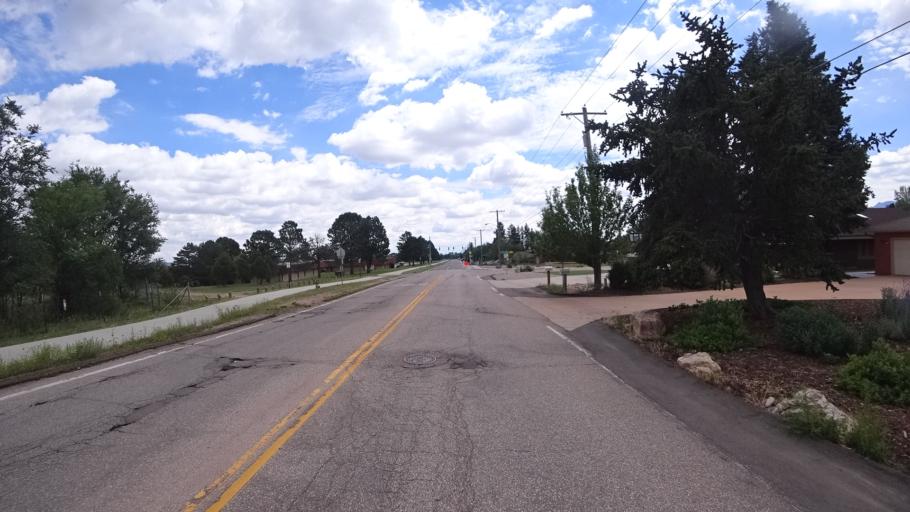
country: US
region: Colorado
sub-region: El Paso County
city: Colorado Springs
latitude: 38.8683
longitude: -104.8584
